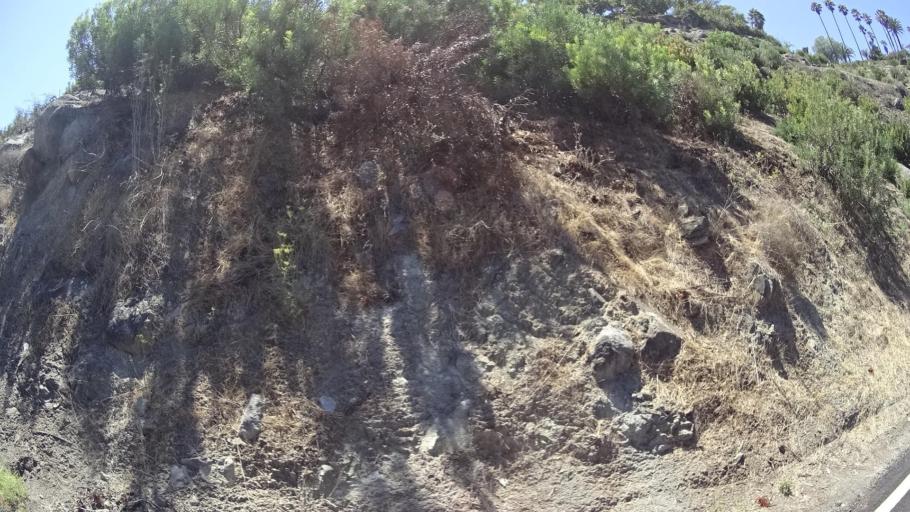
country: US
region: California
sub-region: San Diego County
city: Rainbow
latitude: 33.3826
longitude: -117.1189
